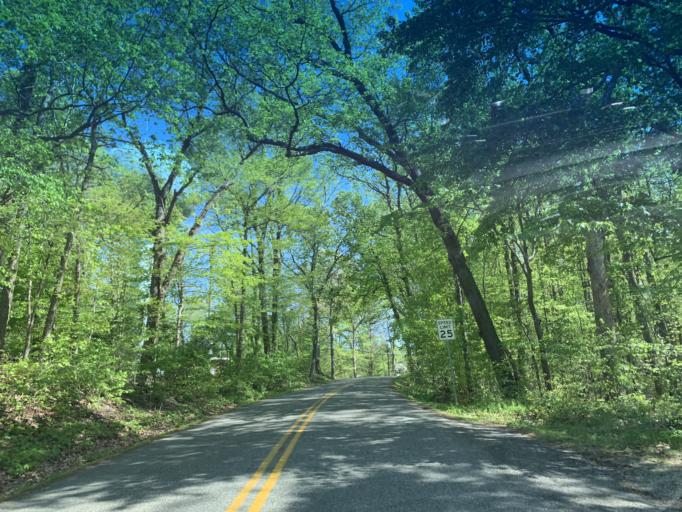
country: US
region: Maryland
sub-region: Harford County
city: Riverside
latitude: 39.4549
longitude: -76.2668
